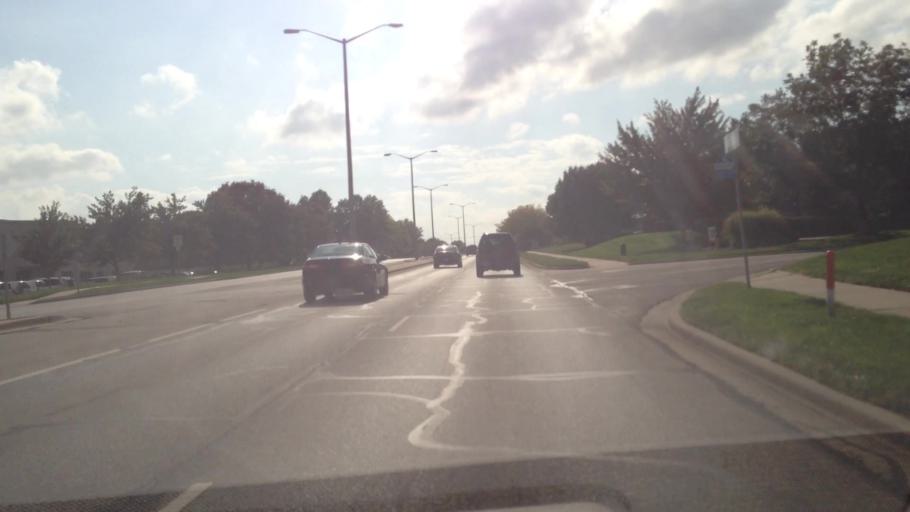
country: US
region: Kansas
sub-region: Johnson County
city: Lenexa
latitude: 38.9232
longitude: -94.7566
